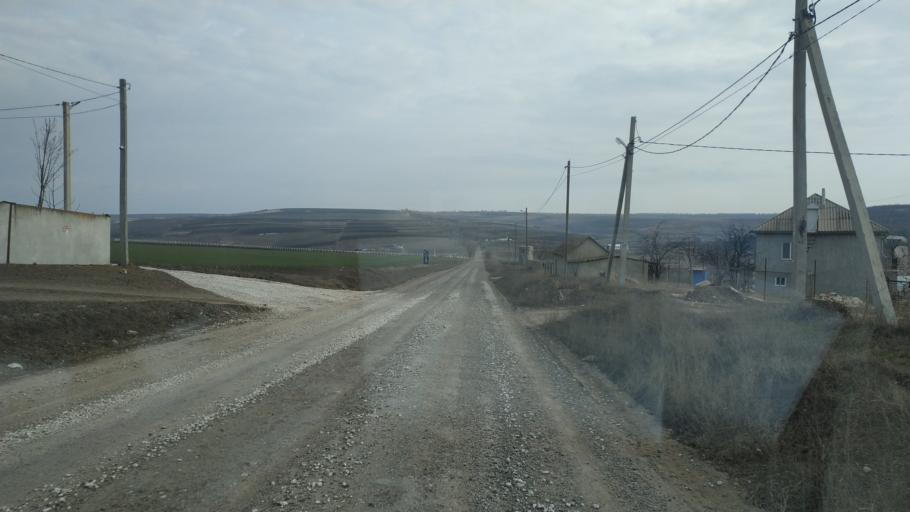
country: MD
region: Chisinau
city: Singera
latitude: 46.9699
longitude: 29.0676
